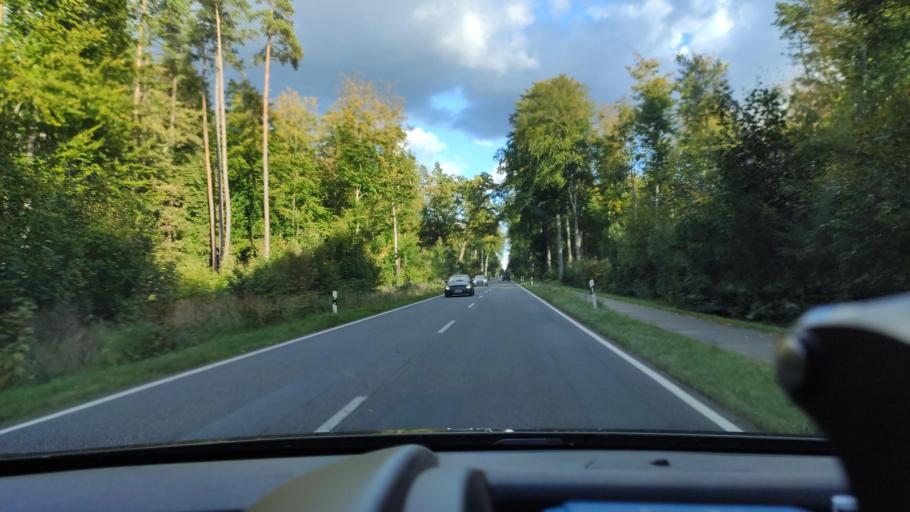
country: DE
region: Mecklenburg-Vorpommern
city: Muhl Rosin
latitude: 53.7689
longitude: 12.2715
